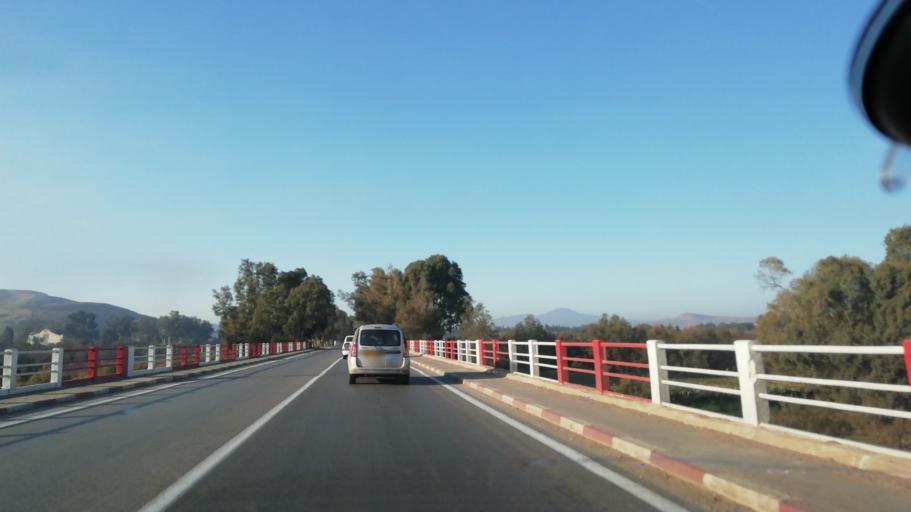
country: DZ
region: Tlemcen
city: Remchi
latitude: 35.0758
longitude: -1.4523
